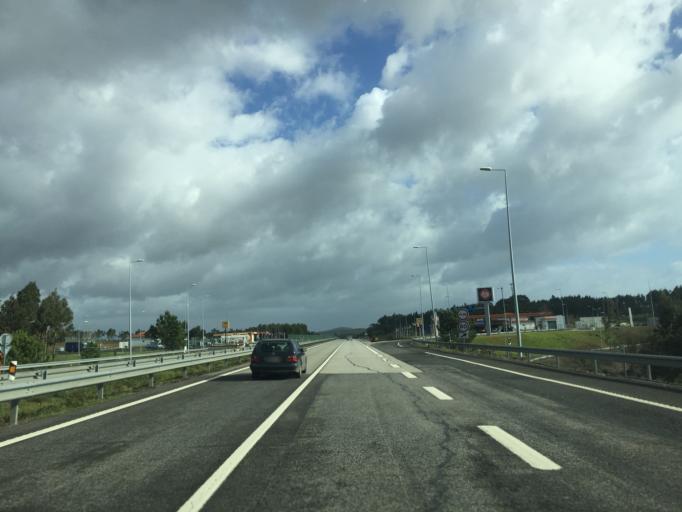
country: PT
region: Lisbon
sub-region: Torres Vedras
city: A dos Cunhados
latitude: 39.1535
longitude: -9.2343
